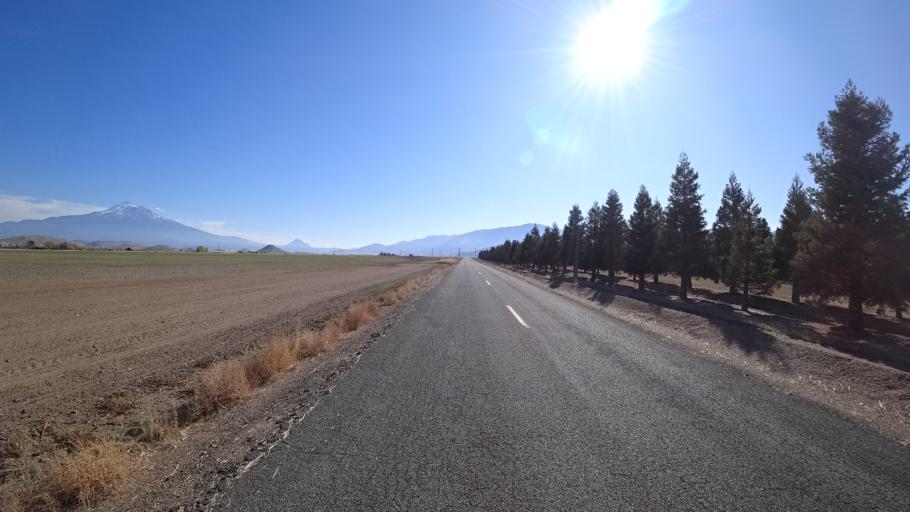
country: US
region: California
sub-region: Siskiyou County
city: Montague
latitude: 41.5549
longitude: -122.5456
